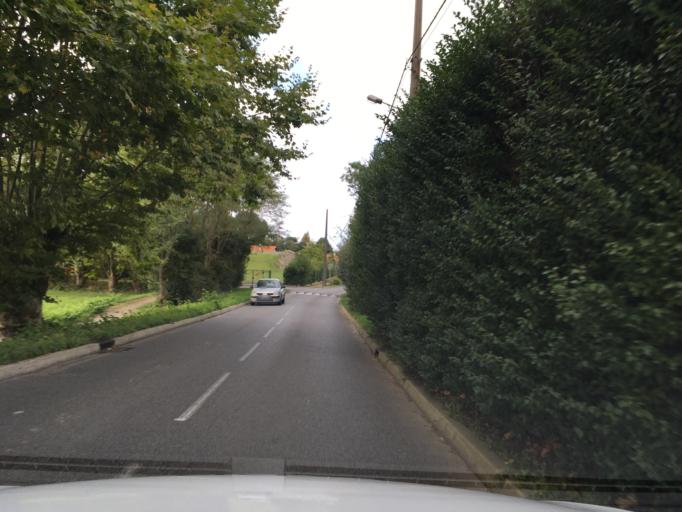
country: FR
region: Aquitaine
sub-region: Departement des Pyrenees-Atlantiques
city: Bassussarry
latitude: 43.4533
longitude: -1.4976
